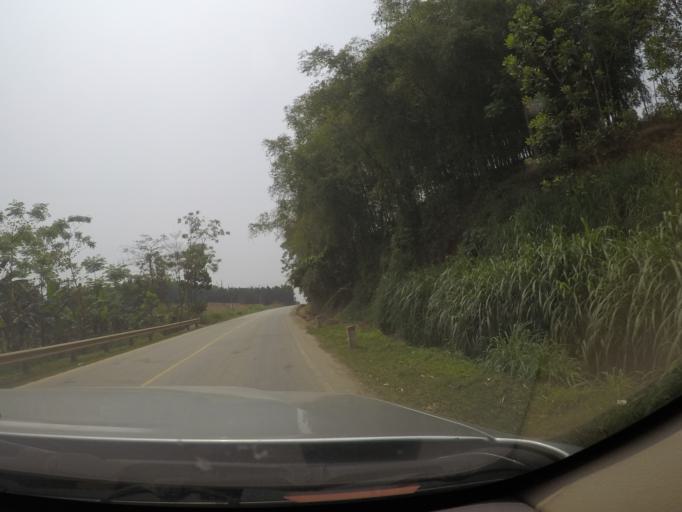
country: VN
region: Thanh Hoa
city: Thi Tran Thuong Xuan
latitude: 19.8627
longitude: 105.4113
